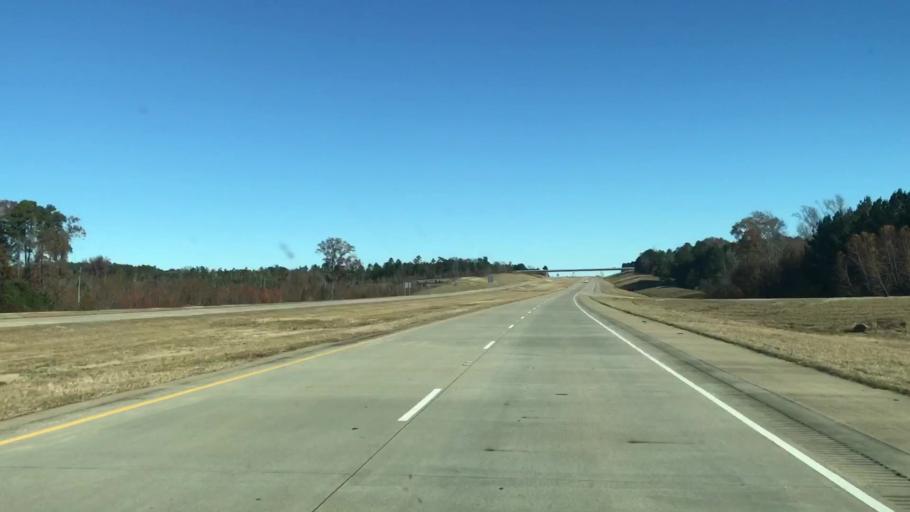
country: US
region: Louisiana
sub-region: Caddo Parish
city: Vivian
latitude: 32.9996
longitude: -93.9084
